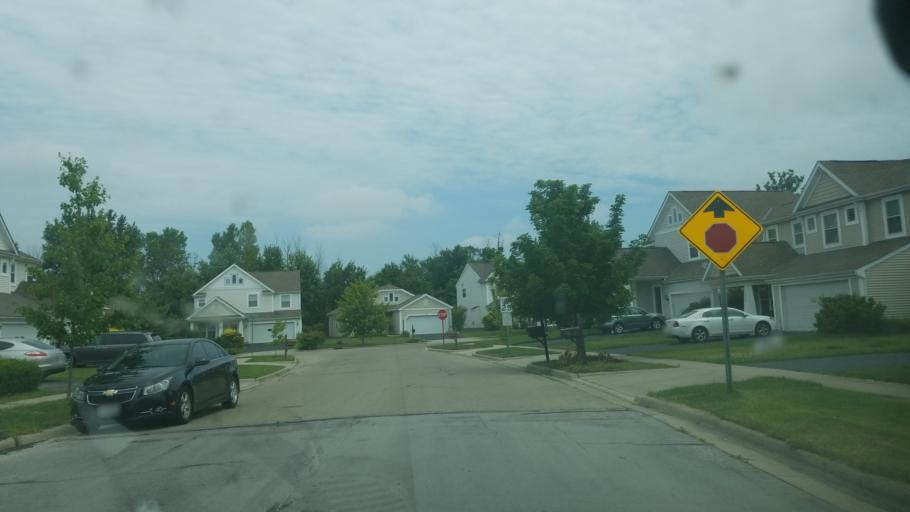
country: US
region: Ohio
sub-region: Franklin County
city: Reynoldsburg
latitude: 40.0095
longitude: -82.7855
